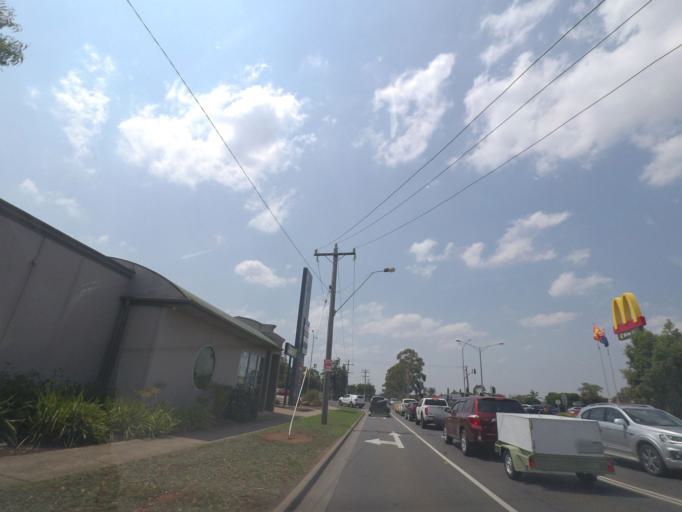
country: AU
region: Victoria
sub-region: Melton
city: Melton West
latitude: -37.6875
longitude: 144.5668
